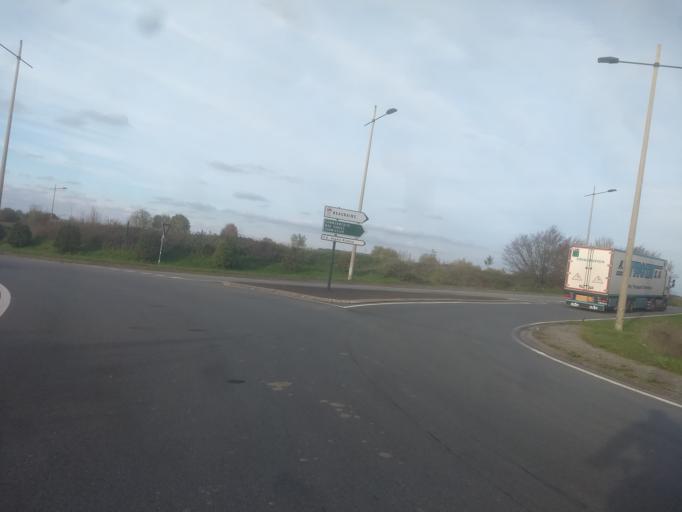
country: FR
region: Nord-Pas-de-Calais
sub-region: Departement du Pas-de-Calais
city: Agny
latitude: 50.2529
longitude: 2.7728
